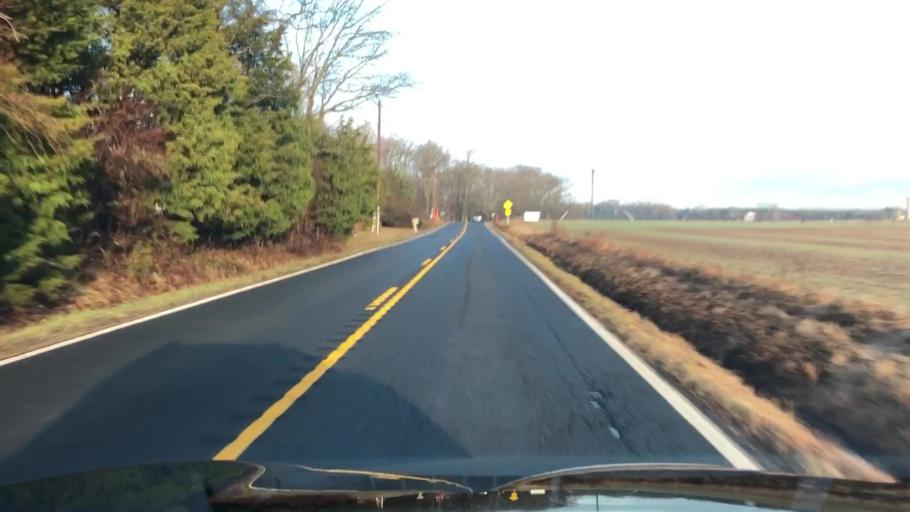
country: US
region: Virginia
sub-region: Fauquier County
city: Bealeton
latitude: 38.5798
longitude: -77.6945
